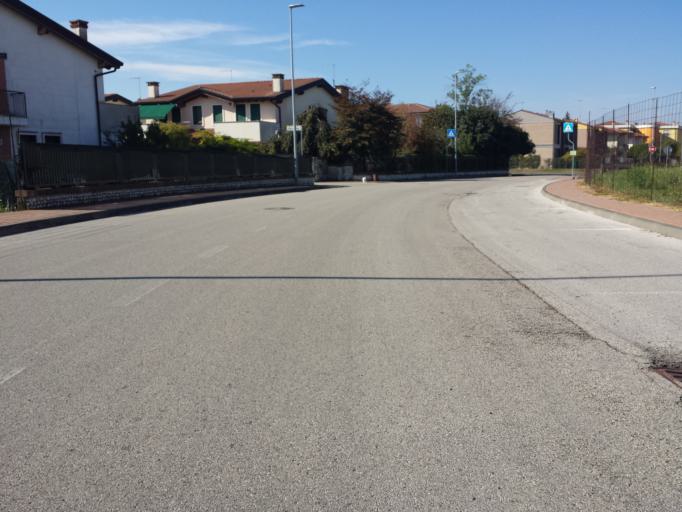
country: IT
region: Veneto
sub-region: Provincia di Vicenza
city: Sandrigo
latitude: 45.6597
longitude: 11.5968
